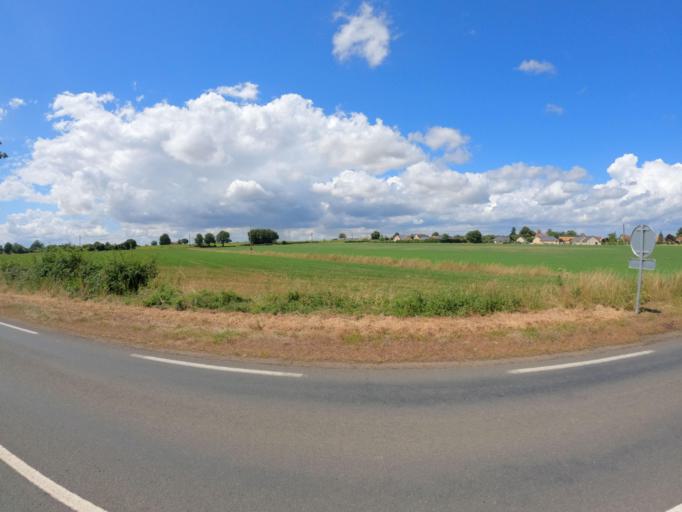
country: FR
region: Pays de la Loire
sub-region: Departement de la Sarthe
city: Brulon
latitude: 47.9511
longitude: -0.2481
